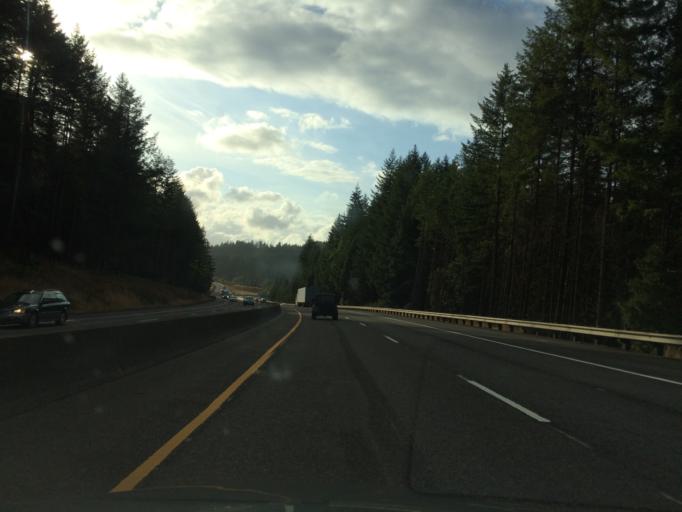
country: US
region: Oregon
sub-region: Douglas County
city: Drain
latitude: 43.7060
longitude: -123.2089
